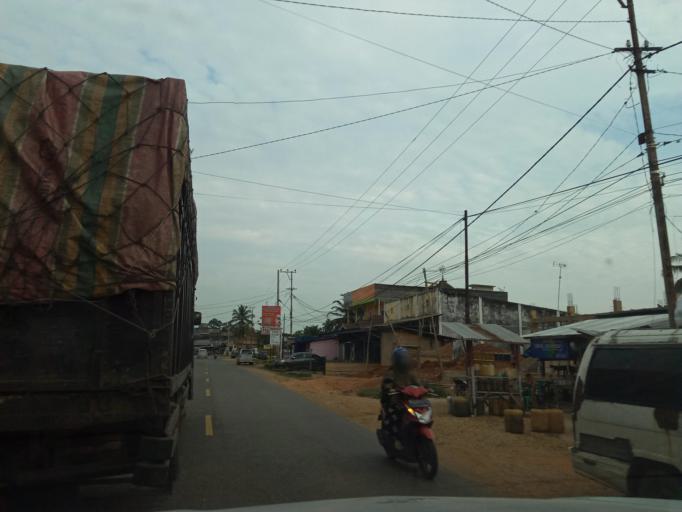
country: ID
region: Jambi
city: Muara Tembesi
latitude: -1.7216
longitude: 103.1339
